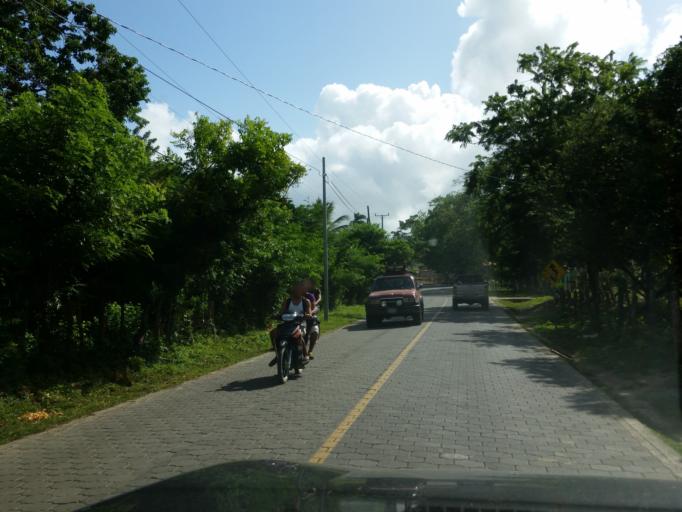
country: NI
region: Rivas
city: San Juan del Sur
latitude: 11.2545
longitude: -85.8588
